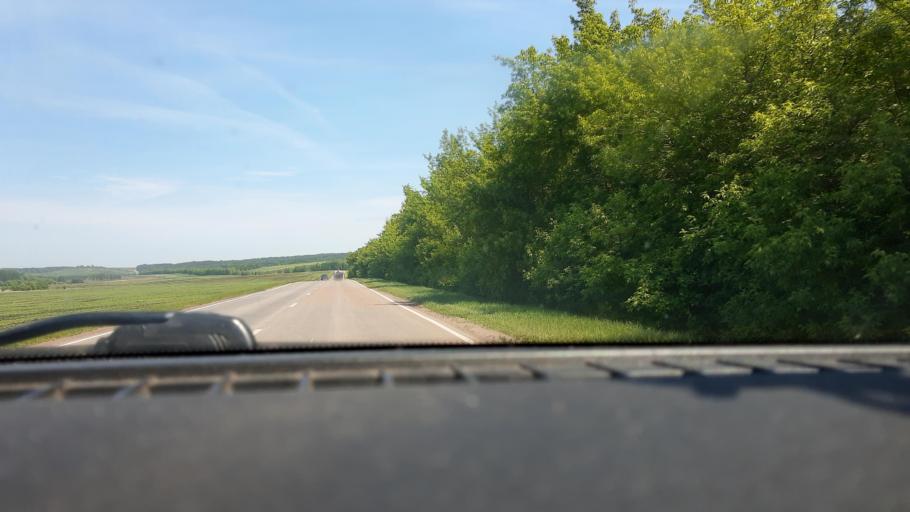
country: RU
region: Bashkortostan
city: Avdon
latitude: 54.4347
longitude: 55.8290
